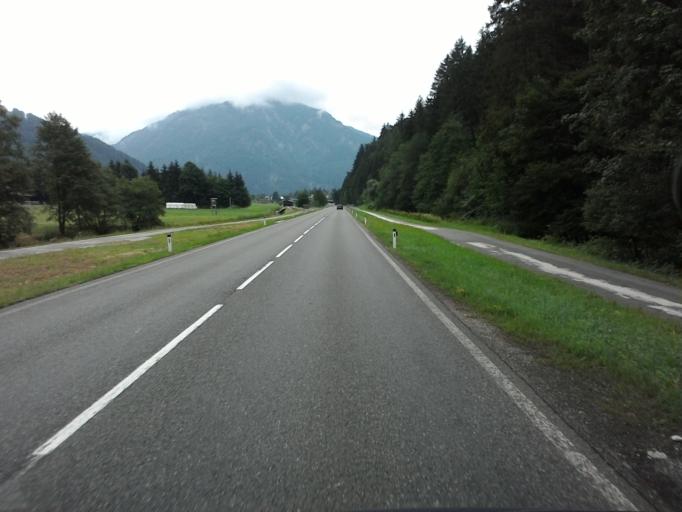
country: AT
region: Tyrol
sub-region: Politischer Bezirk Kitzbuhel
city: Kirchdorf in Tirol
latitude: 47.5597
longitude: 12.4616
